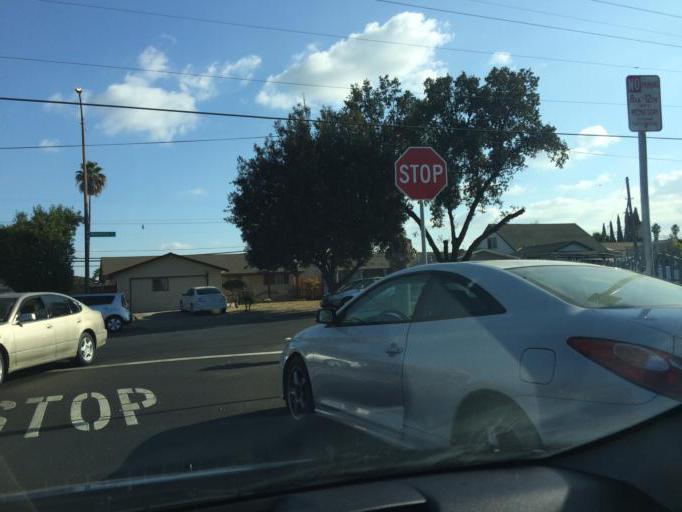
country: US
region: California
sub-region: Santa Clara County
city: Alum Rock
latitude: 37.3312
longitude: -121.8217
